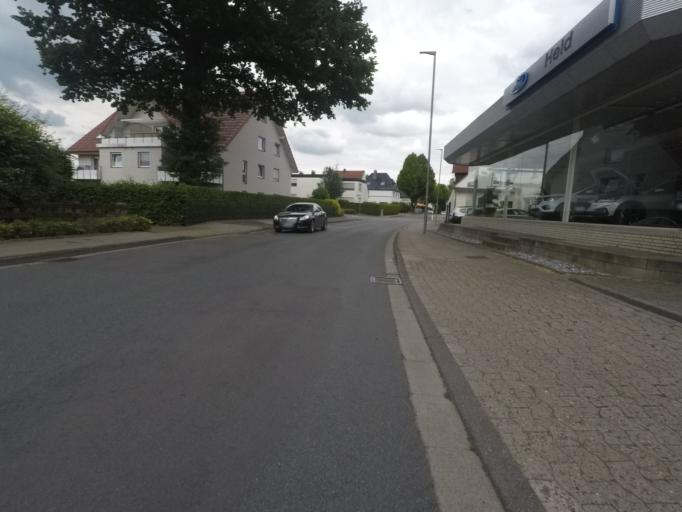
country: DE
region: North Rhine-Westphalia
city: Spenge
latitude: 52.1410
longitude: 8.4925
